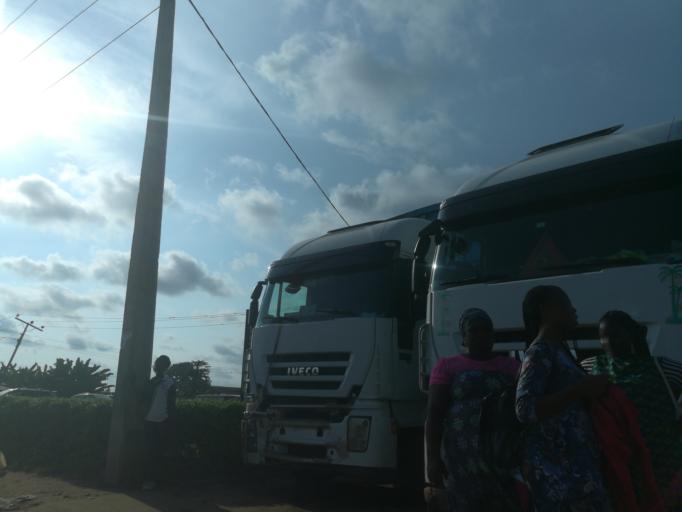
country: NG
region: Ogun
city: Ado Odo
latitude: 6.4958
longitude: 3.0854
